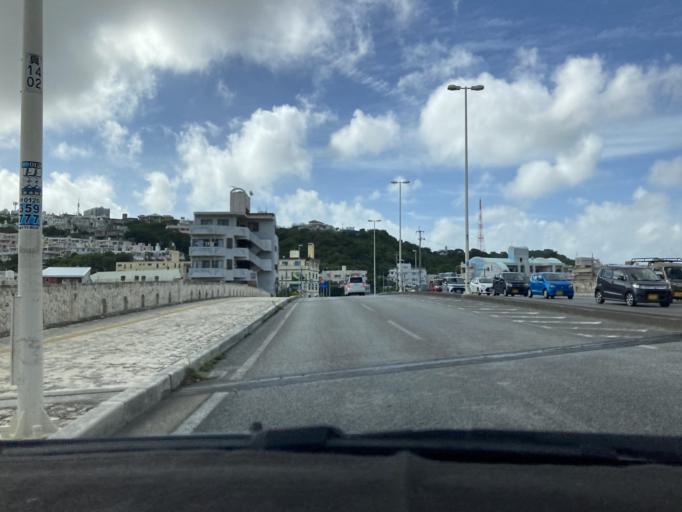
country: JP
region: Okinawa
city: Tomigusuku
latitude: 26.1958
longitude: 127.6954
